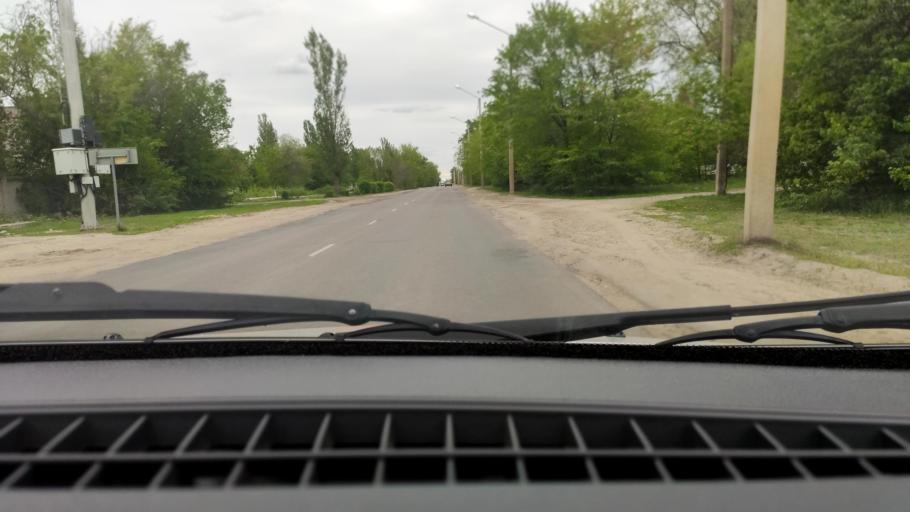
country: RU
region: Voronezj
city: Shilovo
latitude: 51.5690
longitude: 39.1301
